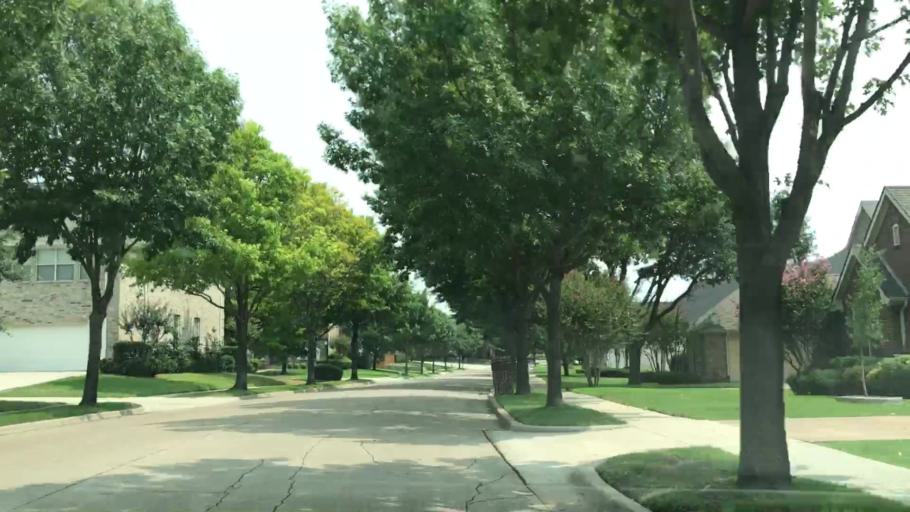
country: US
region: Texas
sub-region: Dallas County
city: Coppell
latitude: 32.9143
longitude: -96.9682
